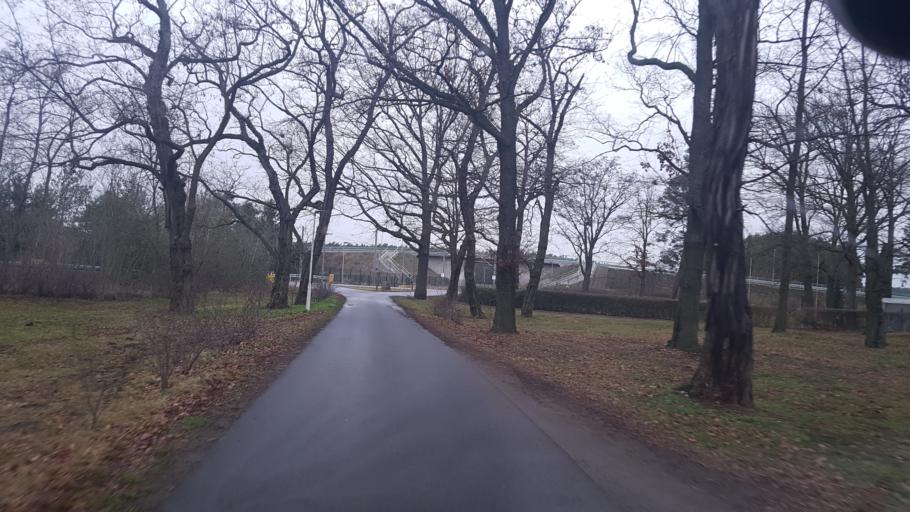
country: DE
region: Brandenburg
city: Ruckersdorf
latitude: 51.5757
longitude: 13.5744
